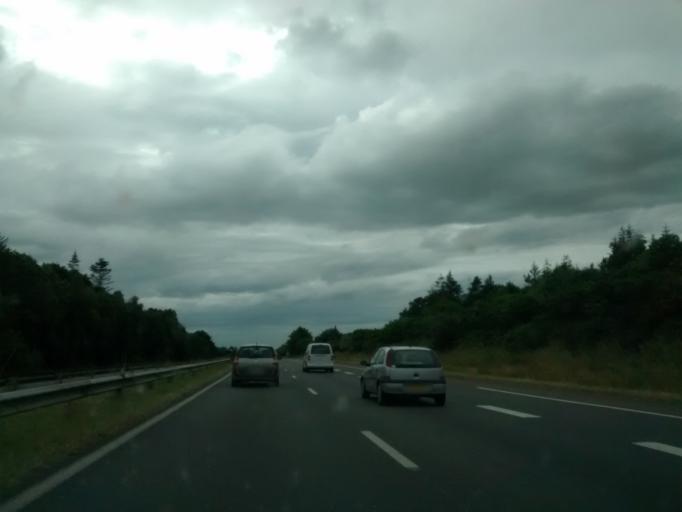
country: FR
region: Brittany
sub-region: Departement des Cotes-d'Armor
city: Plestan
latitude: 48.4092
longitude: -2.4223
